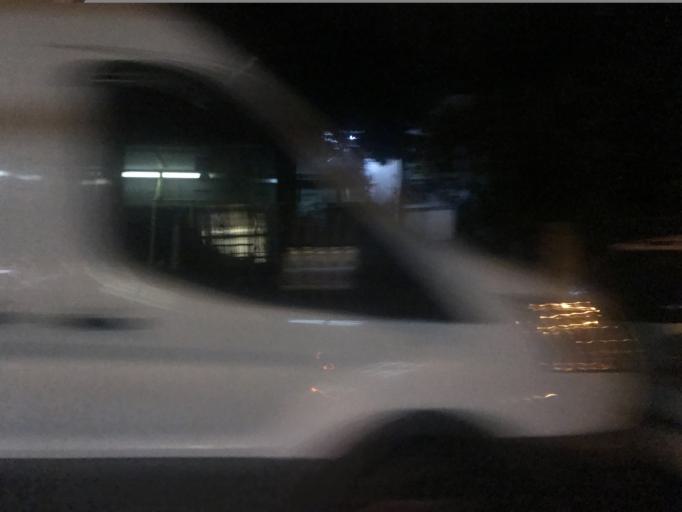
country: TR
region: Istanbul
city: Bahcelievler
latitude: 40.9819
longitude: 28.8679
